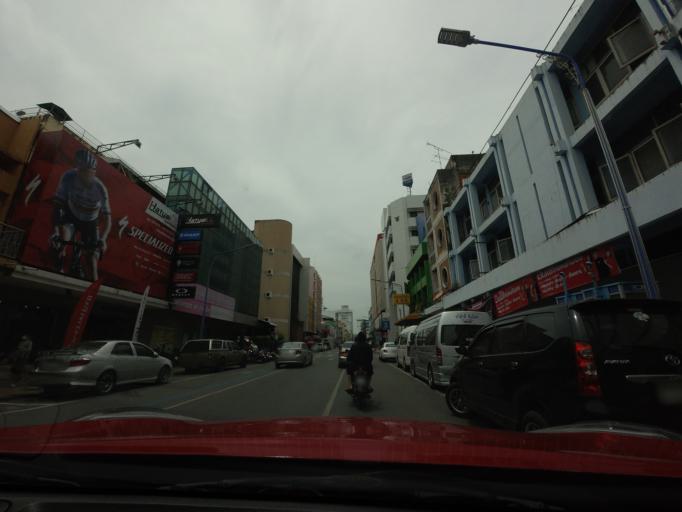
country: TH
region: Songkhla
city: Hat Yai
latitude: 7.0015
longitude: 100.4706
